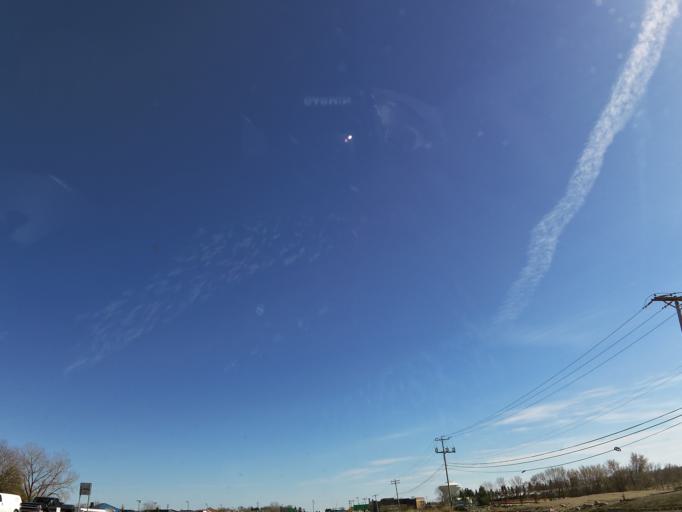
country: US
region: Minnesota
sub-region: Hennepin County
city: Wayzata
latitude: 45.0353
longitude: -93.5124
